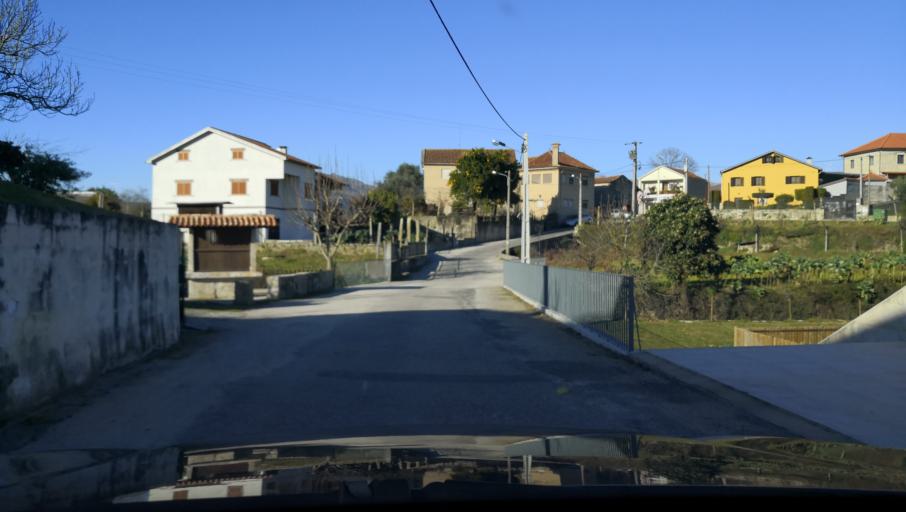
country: PT
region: Viseu
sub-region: Oliveira de Frades
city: Oliveira de Frades
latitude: 40.7338
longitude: -8.1582
